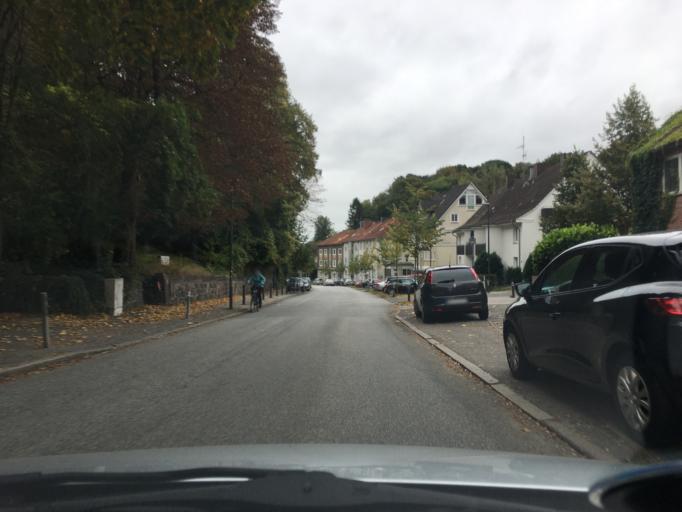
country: DE
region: Schleswig-Holstein
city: Kiel
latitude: 54.3355
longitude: 10.1465
